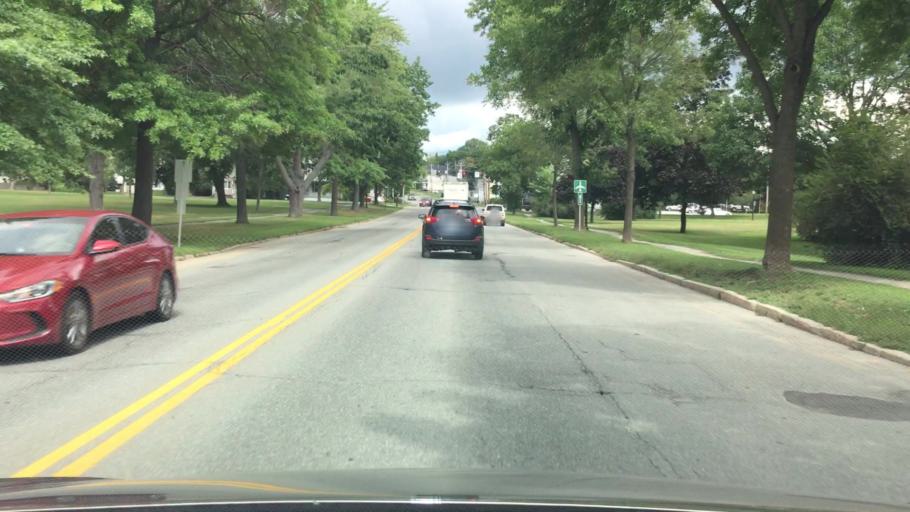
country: US
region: Maine
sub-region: Penobscot County
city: Bangor
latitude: 44.8109
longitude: -68.7697
